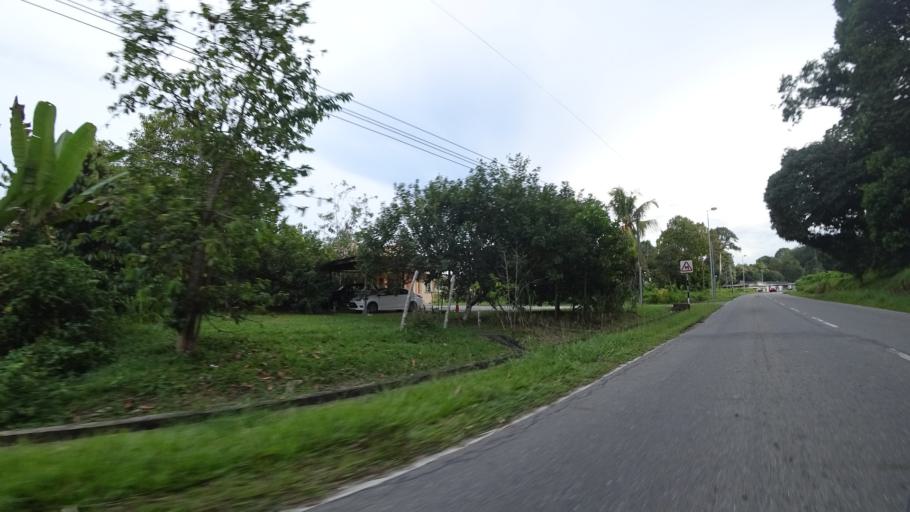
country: BN
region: Brunei and Muara
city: Bandar Seri Begawan
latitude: 4.8519
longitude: 114.8222
